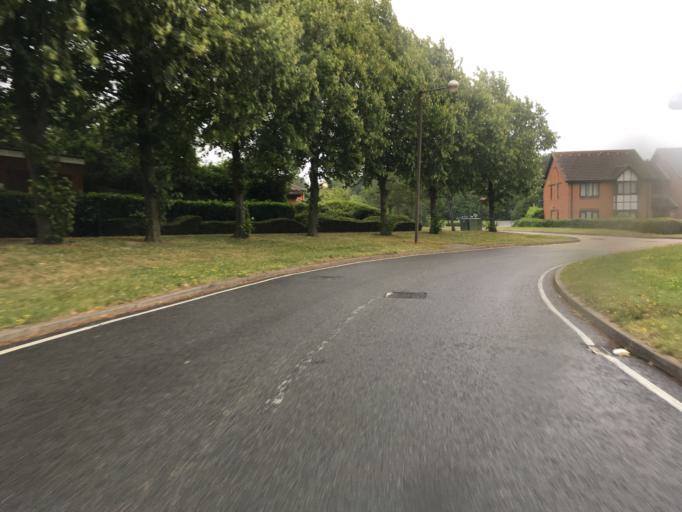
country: GB
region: England
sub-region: Milton Keynes
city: Simpson
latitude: 52.0261
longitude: -0.6956
